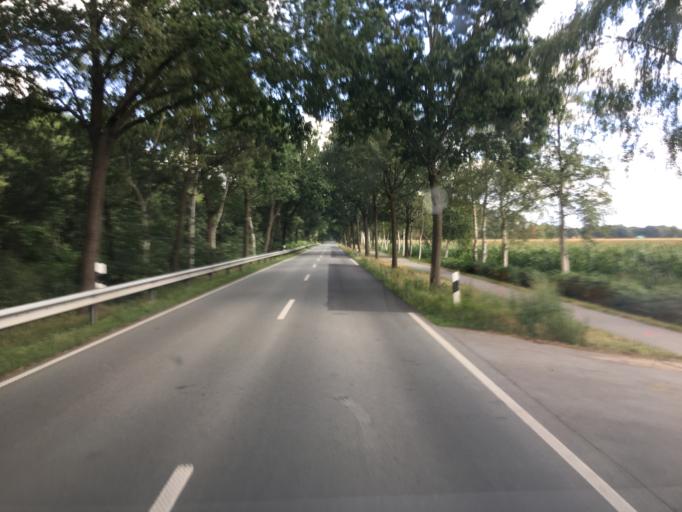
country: DE
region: Lower Saxony
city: Friesoythe
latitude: 53.0850
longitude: 7.8124
